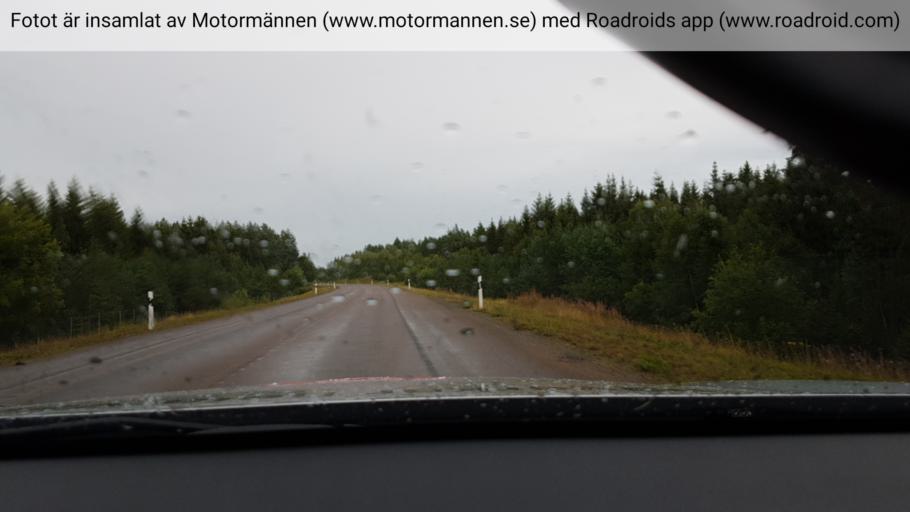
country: SE
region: Uppsala
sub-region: Osthammars Kommun
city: Gimo
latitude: 60.1660
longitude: 18.2603
